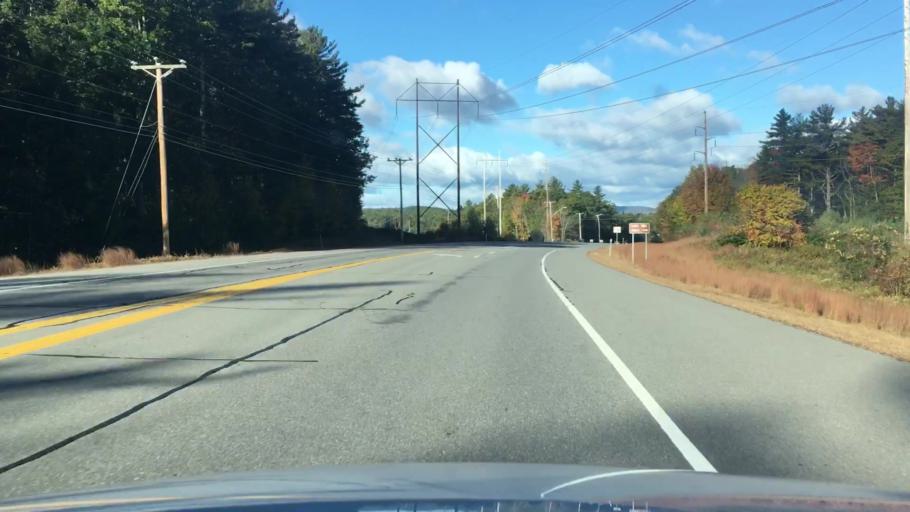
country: US
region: New Hampshire
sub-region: Strafford County
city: Lee
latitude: 43.1541
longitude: -71.0553
